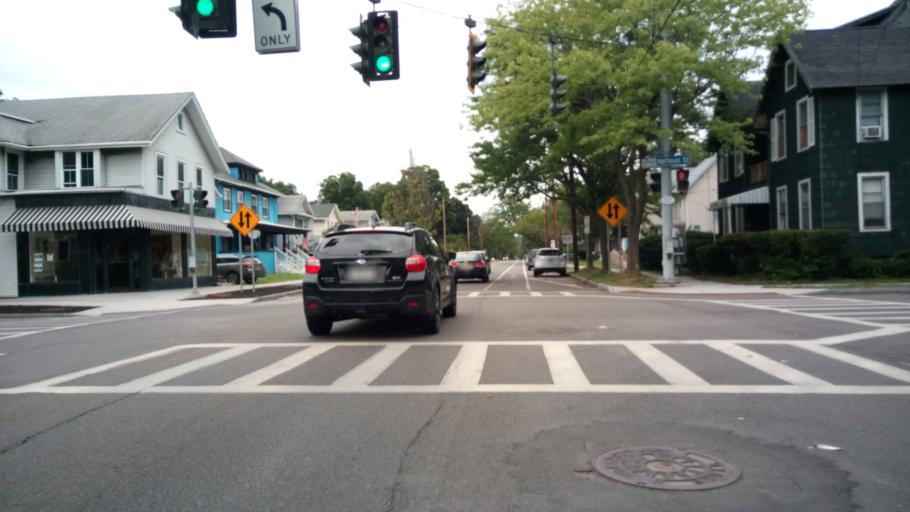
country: US
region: New York
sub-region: Chemung County
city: Elmira
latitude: 42.0836
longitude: -76.8221
